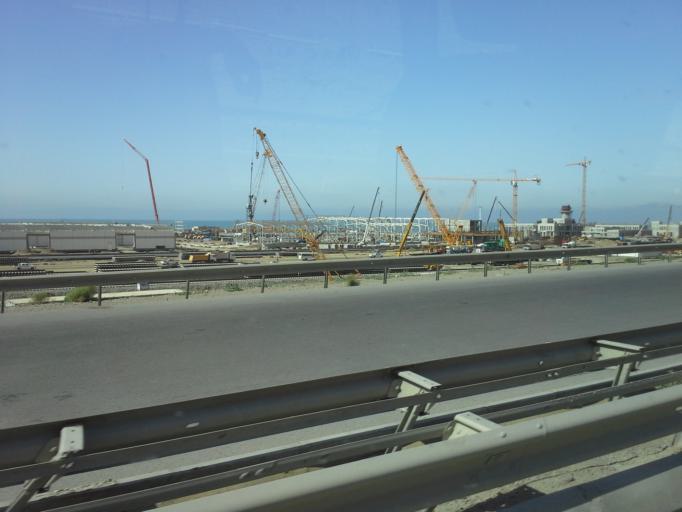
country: TM
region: Balkan
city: Turkmenbasy
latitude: 40.0085
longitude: 53.0293
